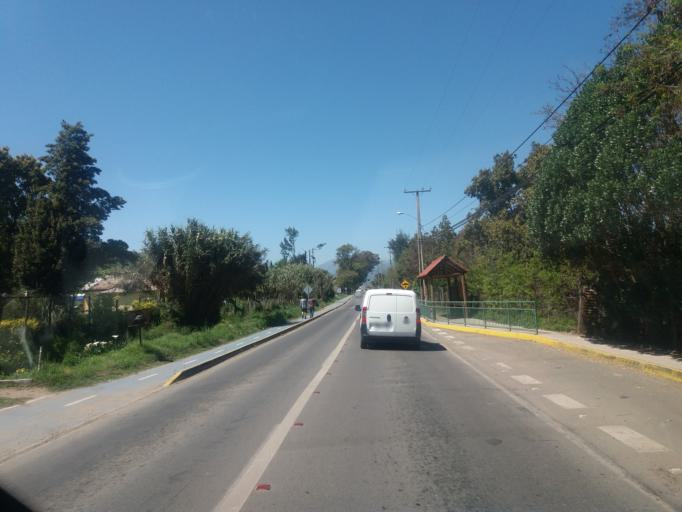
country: CL
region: Valparaiso
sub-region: Provincia de Marga Marga
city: Limache
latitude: -32.9805
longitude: -71.2823
